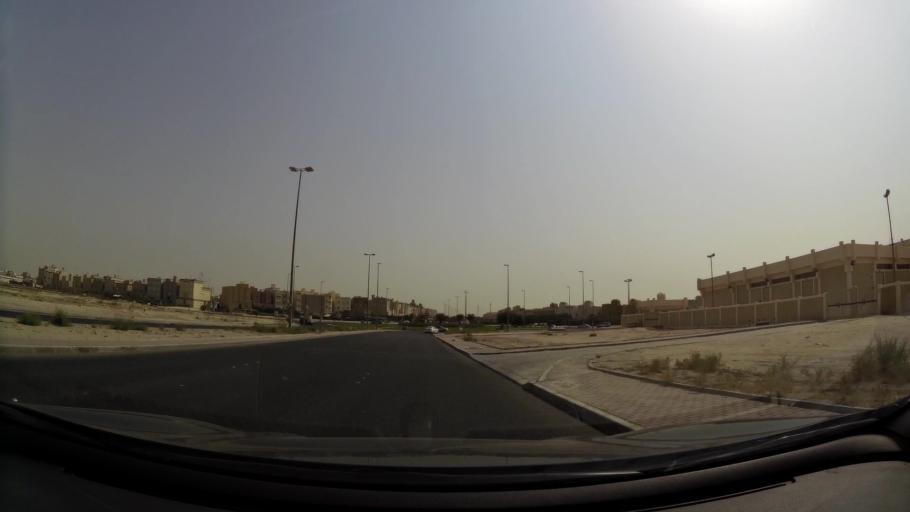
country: KW
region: Muhafazat al Jahra'
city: Al Jahra'
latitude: 29.3226
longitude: 47.7309
